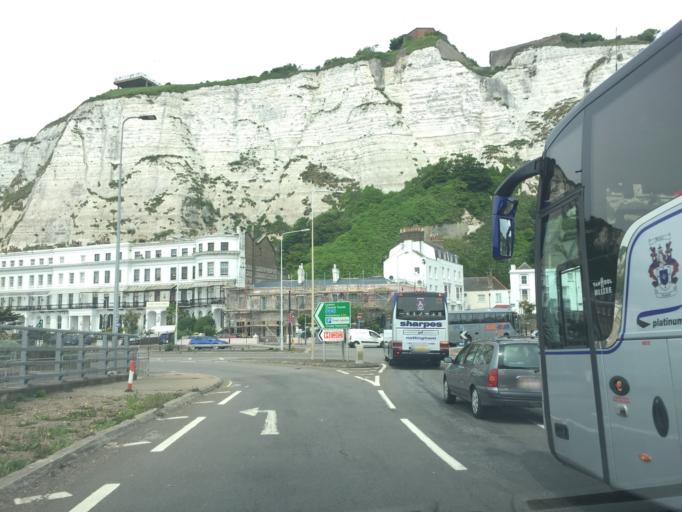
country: GB
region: England
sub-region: Kent
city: Dover
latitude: 51.1258
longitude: 1.3275
